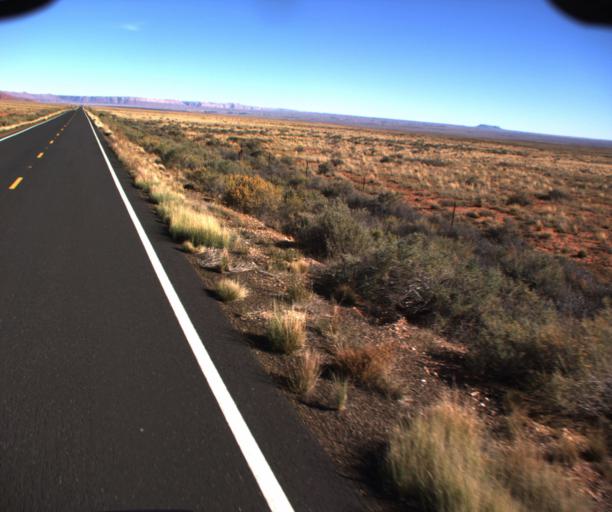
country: US
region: Arizona
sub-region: Coconino County
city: Page
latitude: 36.7118
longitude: -111.9768
